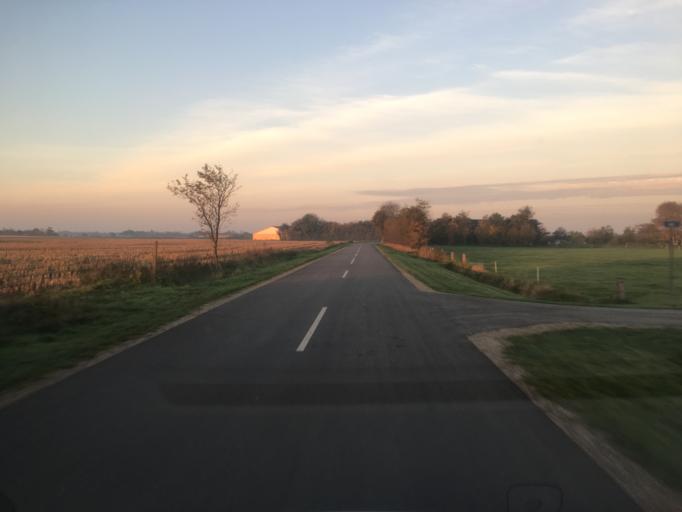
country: DK
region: South Denmark
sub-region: Tonder Kommune
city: Logumkloster
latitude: 55.0607
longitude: 9.0007
